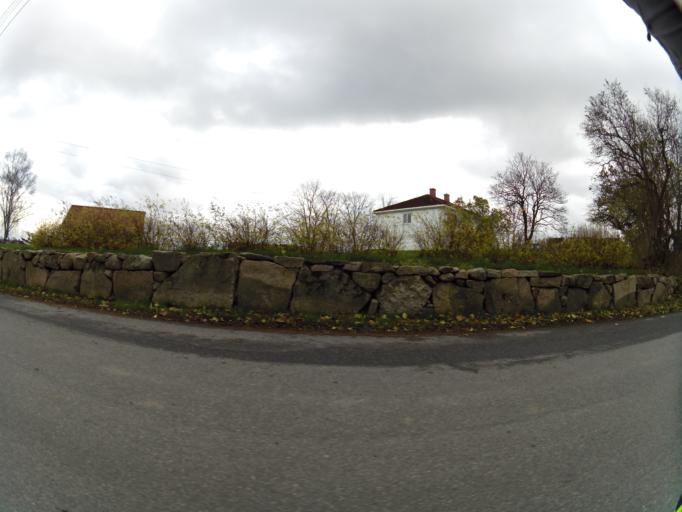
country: NO
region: Ostfold
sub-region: Fredrikstad
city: Fredrikstad
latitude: 59.2627
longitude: 11.0107
